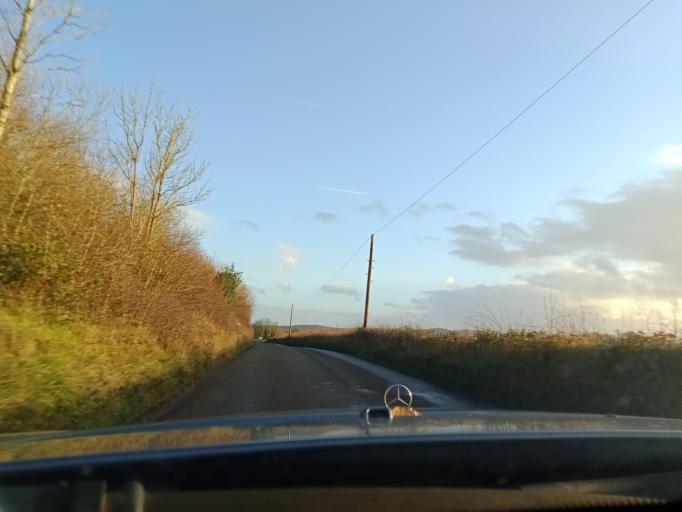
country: IE
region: Leinster
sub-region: Kilkenny
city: Callan
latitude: 52.4912
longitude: -7.3252
